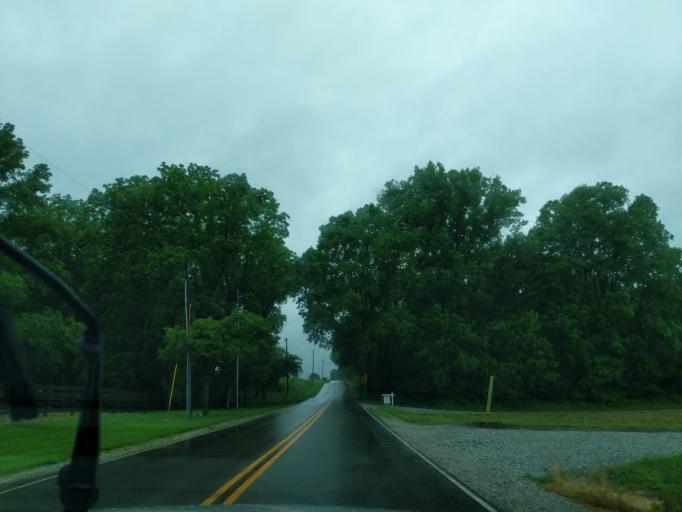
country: US
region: Indiana
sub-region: Madison County
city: Lapel
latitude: 40.0669
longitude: -85.8942
